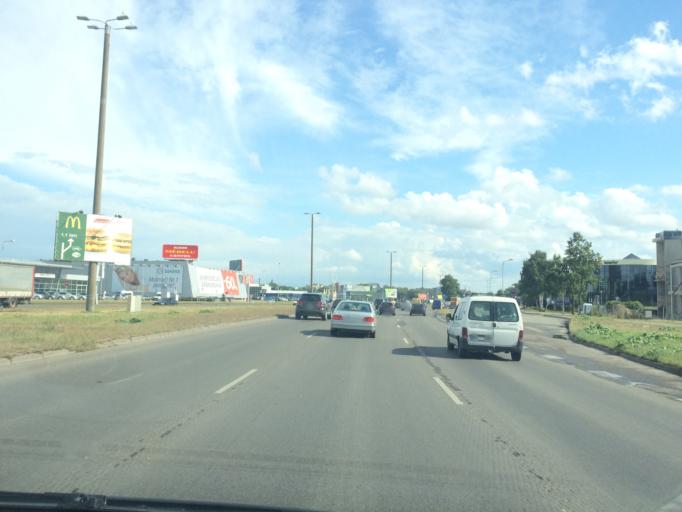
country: LV
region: Riga
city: Riga
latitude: 56.9321
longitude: 24.1481
